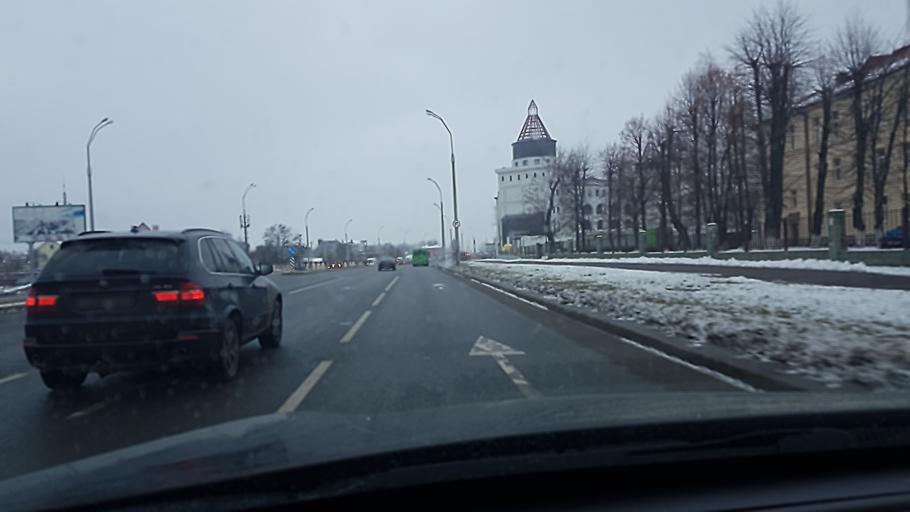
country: BY
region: Minsk
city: Bal'shavik
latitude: 53.9541
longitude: 27.5351
